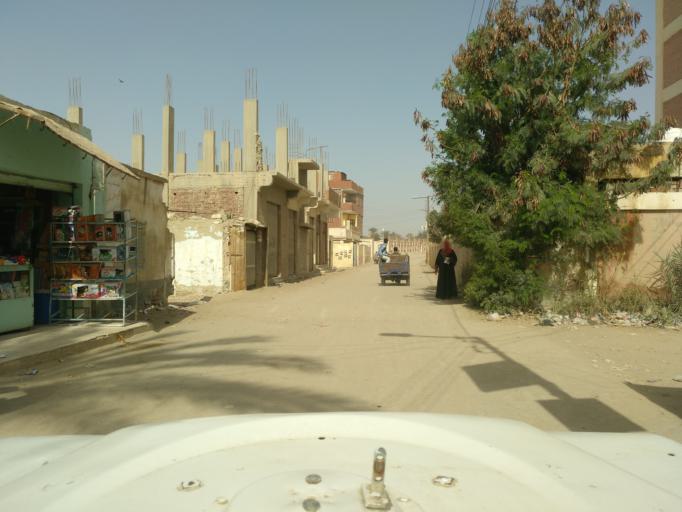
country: EG
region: Al Buhayrah
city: Beheira
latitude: 30.3781
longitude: 30.3467
